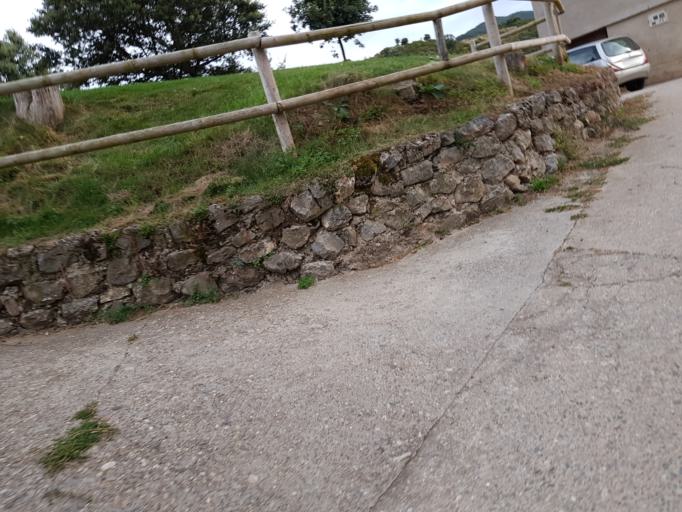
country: ES
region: La Rioja
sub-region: Provincia de La Rioja
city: Torrecilla en Cameros
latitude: 42.2547
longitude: -2.6321
